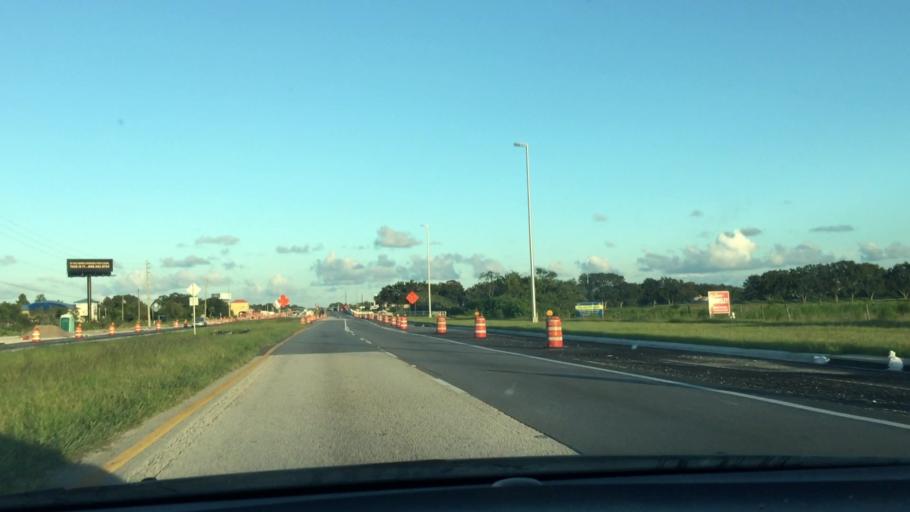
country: US
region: Florida
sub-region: Osceola County
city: Saint Cloud
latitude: 28.2599
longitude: -81.3262
